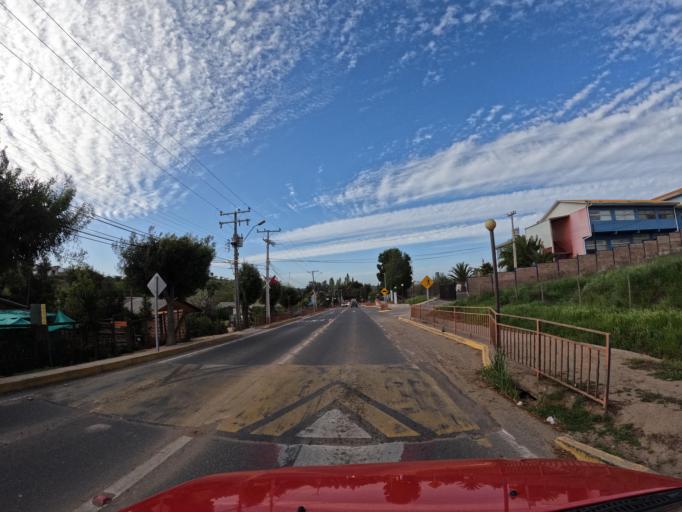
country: CL
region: Valparaiso
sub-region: San Antonio Province
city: San Antonio
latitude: -34.1260
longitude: -71.7268
